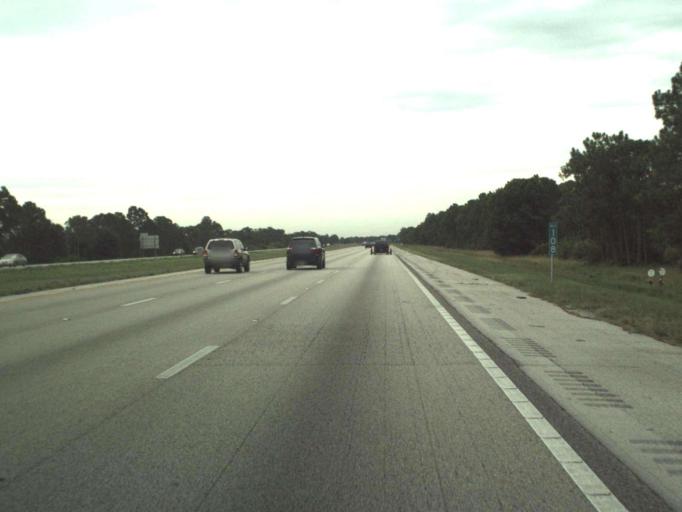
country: US
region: Florida
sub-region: Martin County
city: Palm City
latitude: 27.1392
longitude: -80.3665
